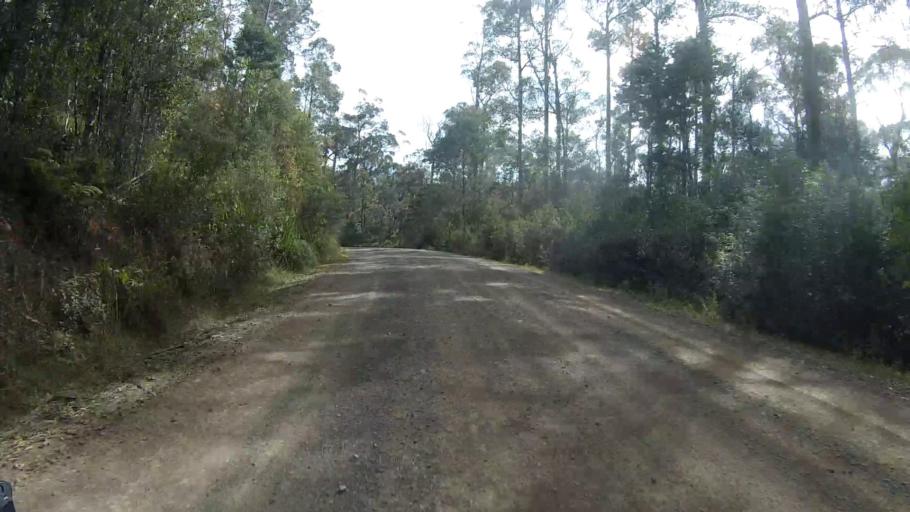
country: AU
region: Tasmania
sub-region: Sorell
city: Sorell
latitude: -42.7380
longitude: 147.8336
